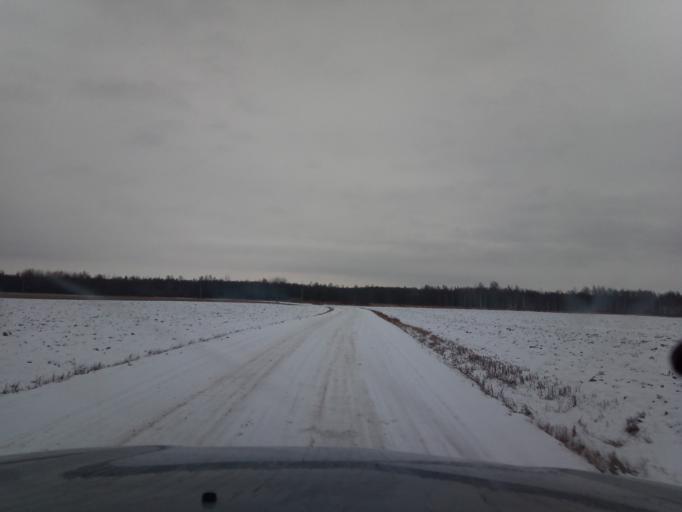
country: LT
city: Ramygala
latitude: 55.4845
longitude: 24.5668
